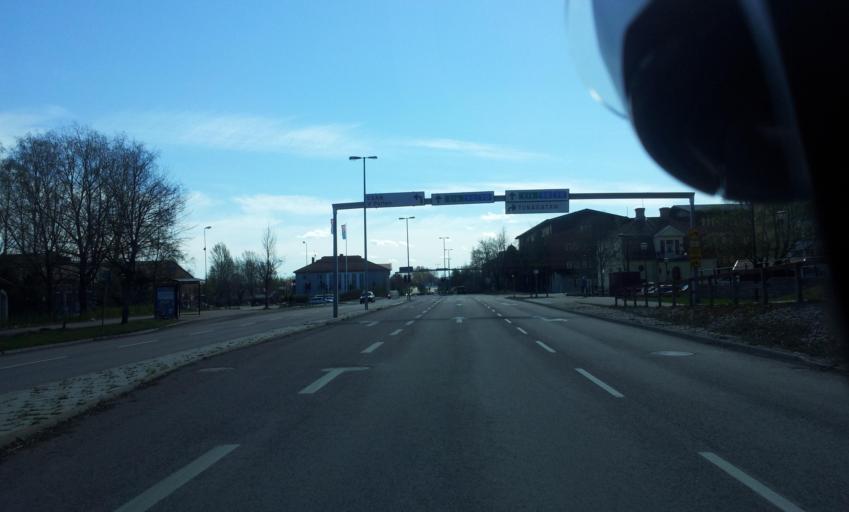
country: SE
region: Dalarna
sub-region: Borlange Kommun
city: Borlaenge
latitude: 60.4871
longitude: 15.4380
